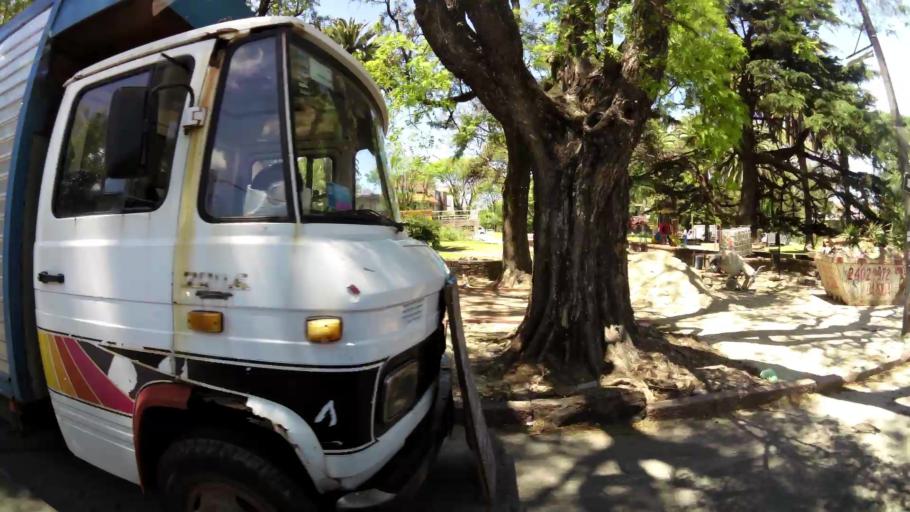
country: UY
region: Canelones
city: Paso de Carrasco
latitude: -34.8938
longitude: -56.1155
